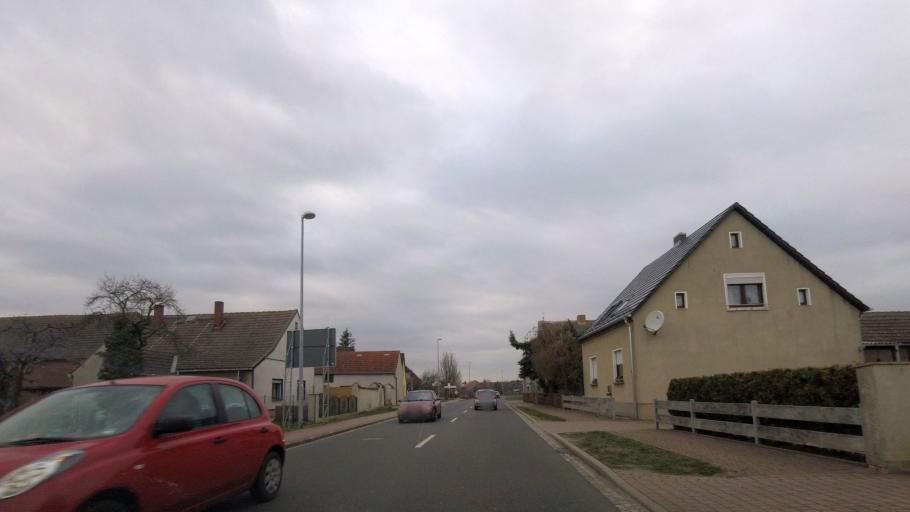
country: DE
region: Saxony-Anhalt
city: Bergwitz
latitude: 51.7919
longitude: 12.6000
